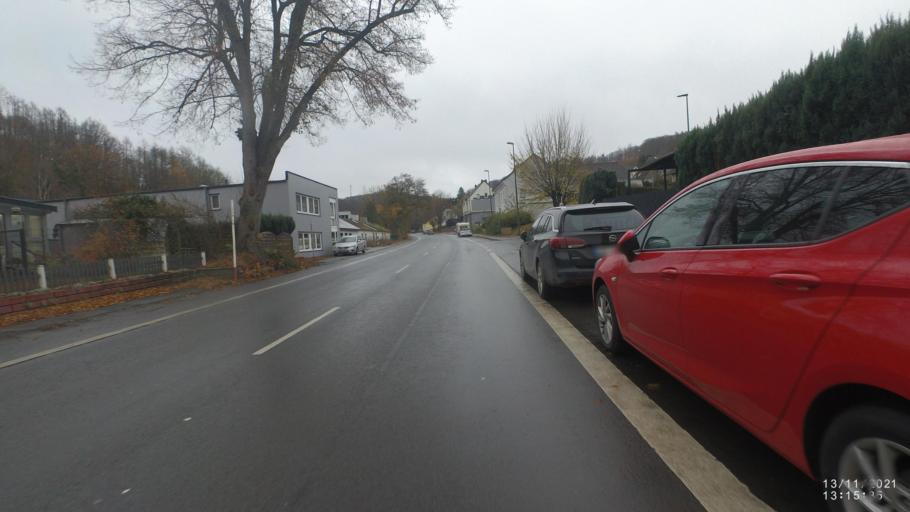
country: DE
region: North Rhine-Westphalia
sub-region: Regierungsbezirk Arnsberg
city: Luedenscheid
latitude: 51.2432
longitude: 7.6221
